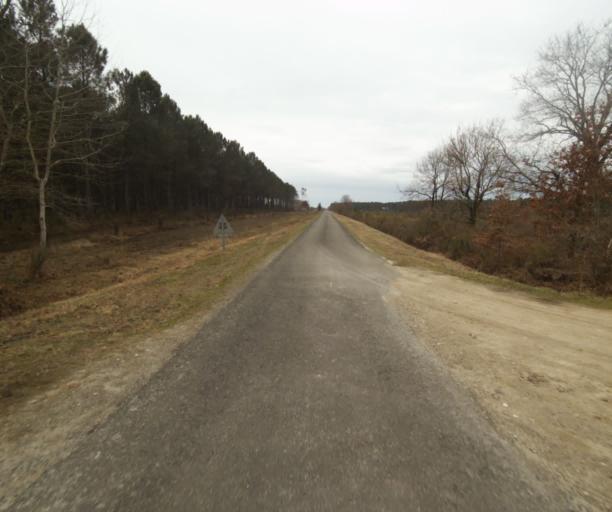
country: FR
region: Aquitaine
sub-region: Departement des Landes
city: Gabarret
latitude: 44.0259
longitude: -0.0531
